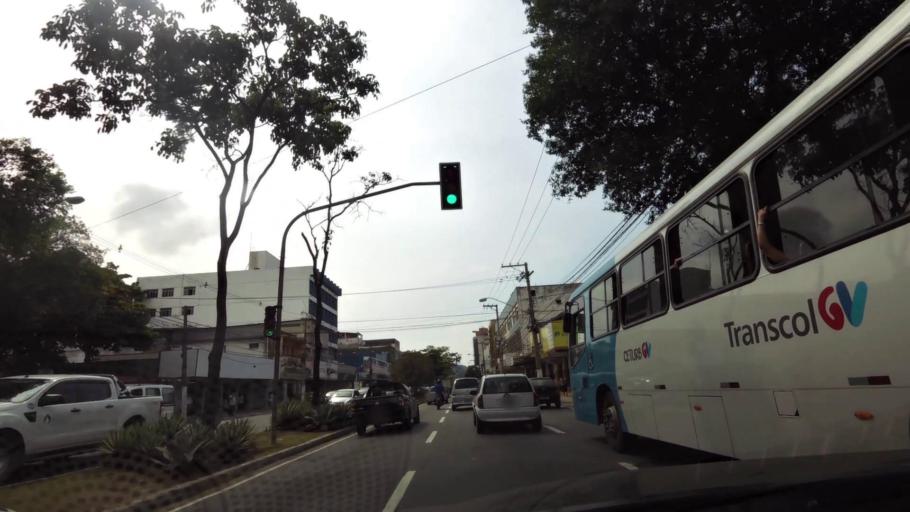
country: BR
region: Espirito Santo
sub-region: Vitoria
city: Vitoria
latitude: -20.3114
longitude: -40.3181
